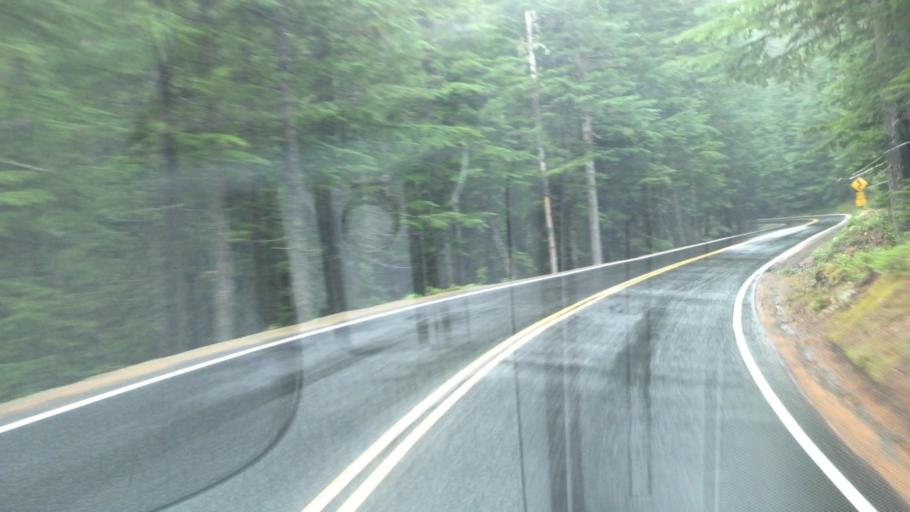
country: US
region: Washington
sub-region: Pierce County
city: Buckley
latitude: 46.7518
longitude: -121.8123
